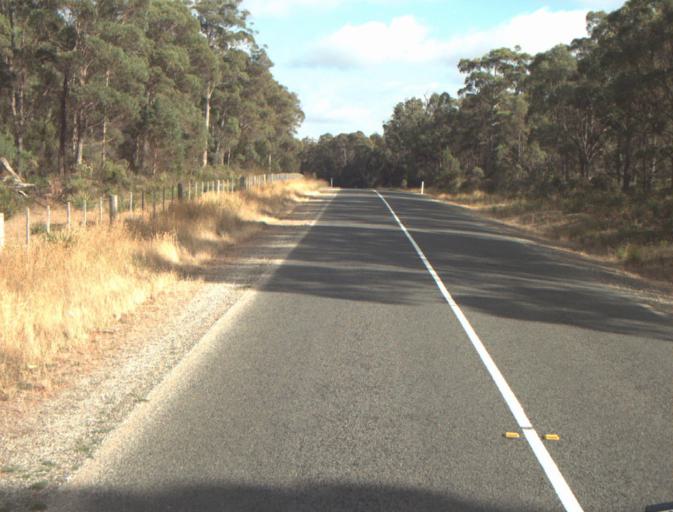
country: AU
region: Tasmania
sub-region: Dorset
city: Bridport
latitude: -41.1285
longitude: 147.2126
